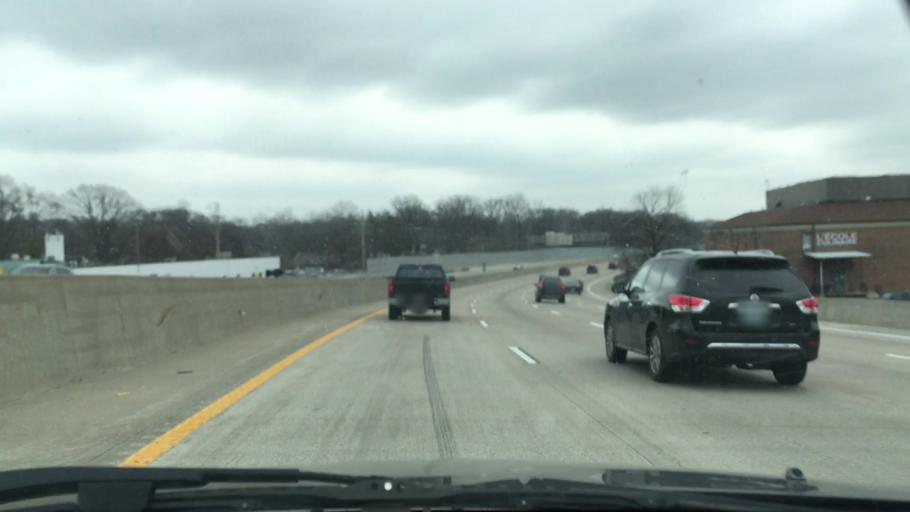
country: US
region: Missouri
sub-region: Saint Louis County
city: Ladue
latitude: 38.6362
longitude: -90.3933
